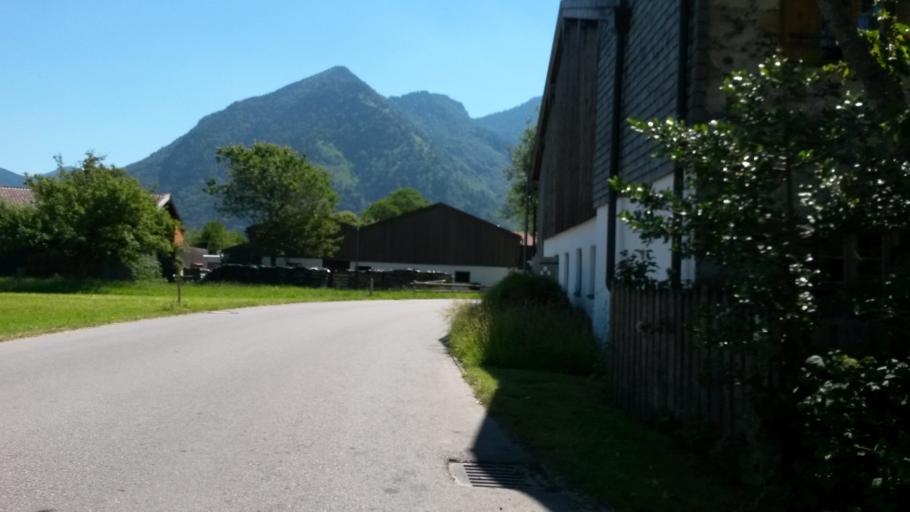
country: DE
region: Bavaria
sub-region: Upper Bavaria
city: Marquartstein
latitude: 47.7635
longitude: 12.4527
